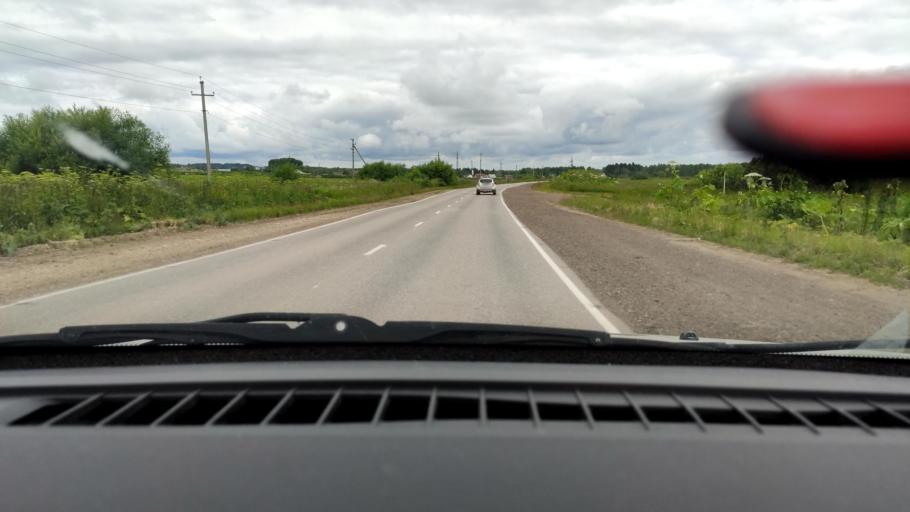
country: RU
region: Perm
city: Ust'-Kachka
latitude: 58.0754
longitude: 55.6203
